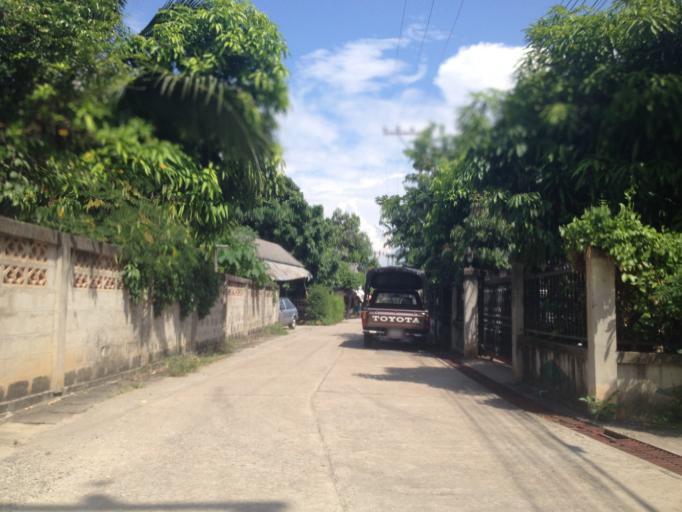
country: TH
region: Chiang Mai
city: Hang Dong
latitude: 18.7256
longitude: 98.9281
